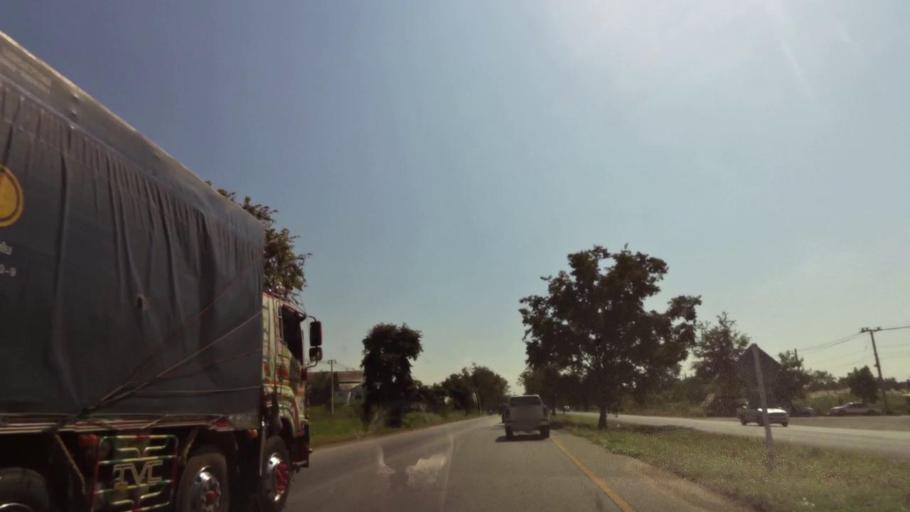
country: TH
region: Nakhon Sawan
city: Kao Liao
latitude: 15.8210
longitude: 100.1194
